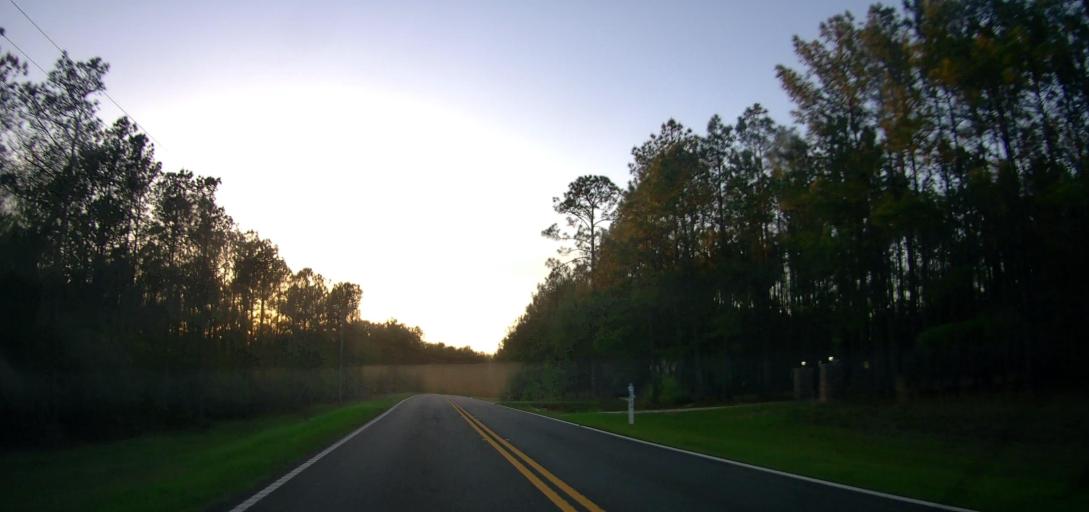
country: US
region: Georgia
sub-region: Marion County
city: Buena Vista
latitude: 32.4269
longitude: -84.5937
